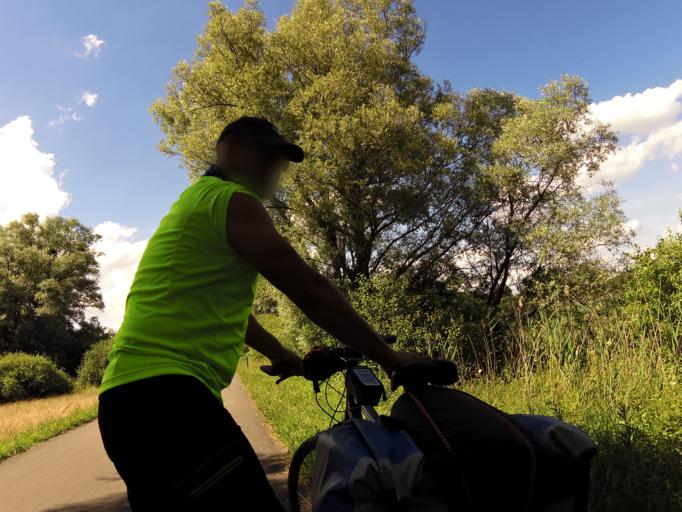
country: DE
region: Baden-Wuerttemberg
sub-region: Freiburg Region
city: Moos
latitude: 47.7343
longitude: 8.9276
